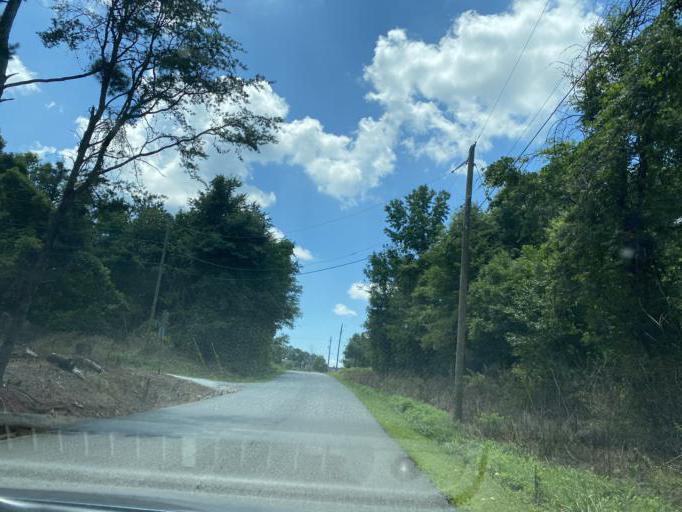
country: US
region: South Carolina
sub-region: Cherokee County
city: Gaffney
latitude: 35.1228
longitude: -81.7226
